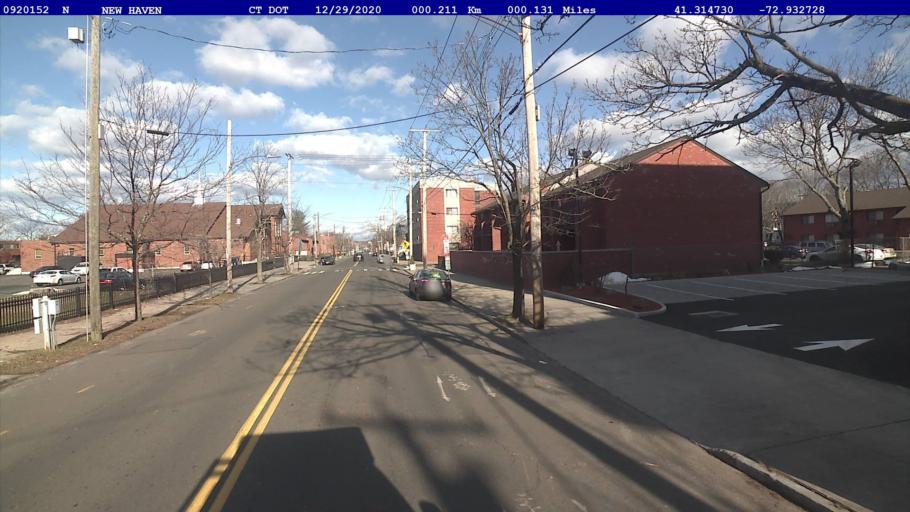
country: US
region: Connecticut
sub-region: New Haven County
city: New Haven
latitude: 41.3147
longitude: -72.9327
